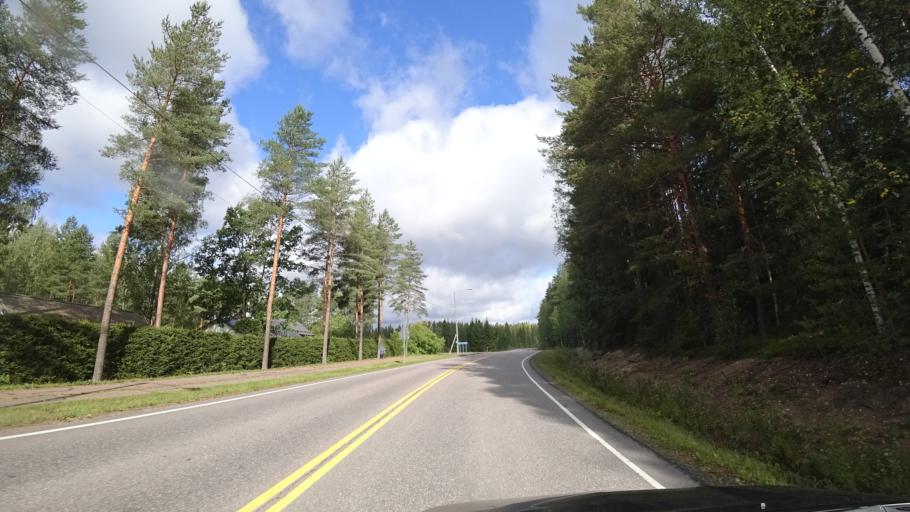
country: FI
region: Uusimaa
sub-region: Helsinki
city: Hyvinge
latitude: 60.6597
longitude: 24.9820
